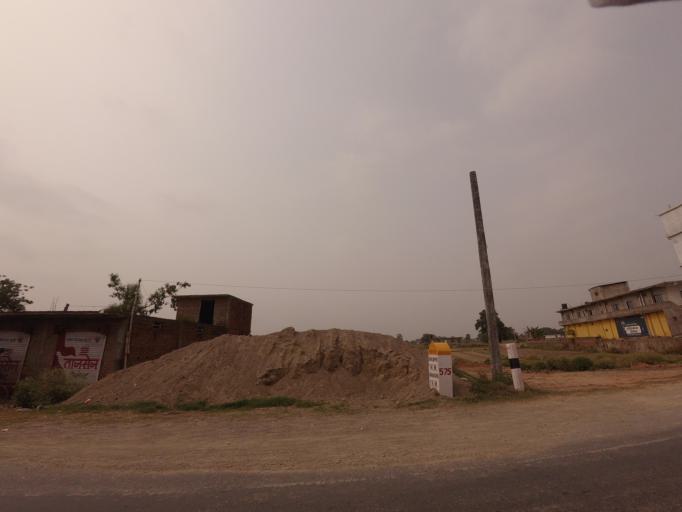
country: IN
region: Uttar Pradesh
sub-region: Maharajganj
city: Nautanwa
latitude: 27.4923
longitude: 83.3153
